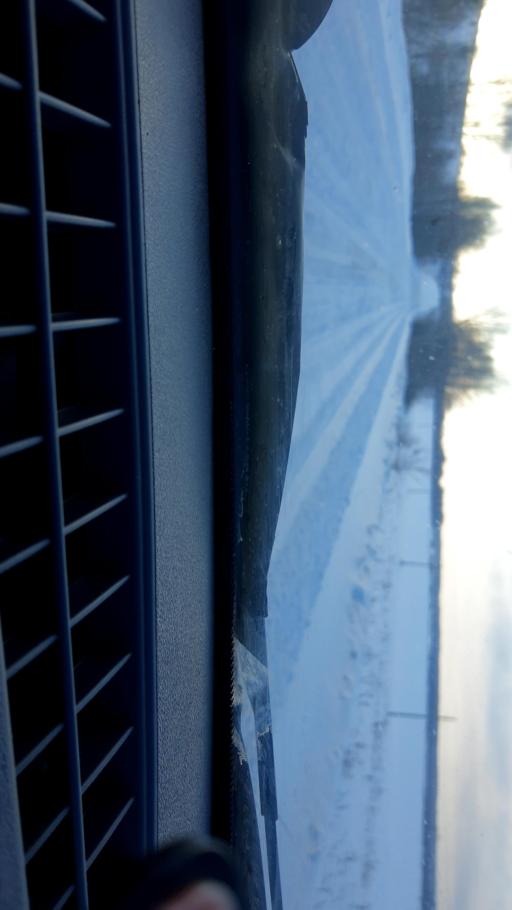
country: RU
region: Bashkortostan
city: Asanovo
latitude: 55.1448
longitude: 55.6423
